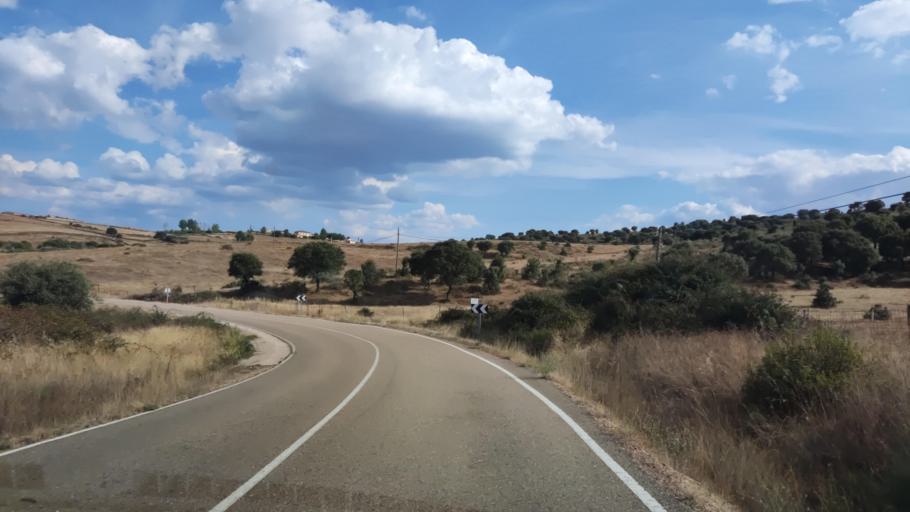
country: ES
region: Castille and Leon
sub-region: Provincia de Salamanca
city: Pastores
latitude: 40.5210
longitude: -6.5172
